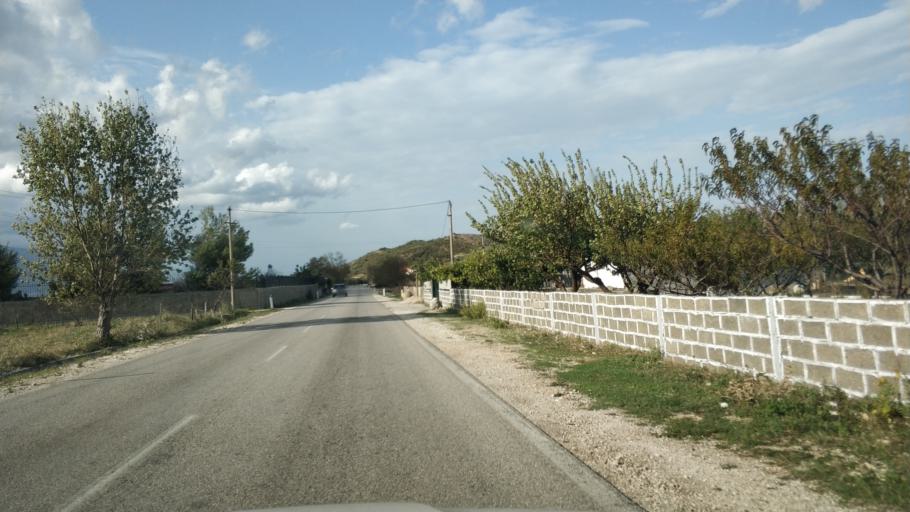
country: AL
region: Vlore
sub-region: Rrethi i Vlores
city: Orikum
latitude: 40.2910
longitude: 19.4921
